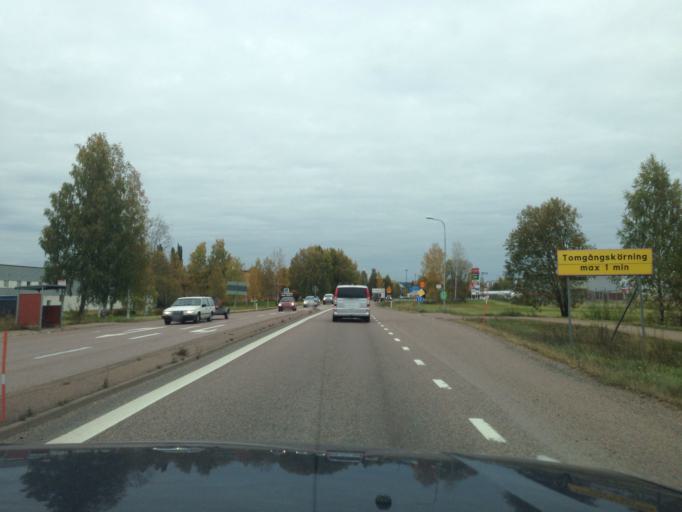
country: SE
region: Dalarna
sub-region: Borlange Kommun
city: Borlaenge
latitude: 60.4771
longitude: 15.4081
